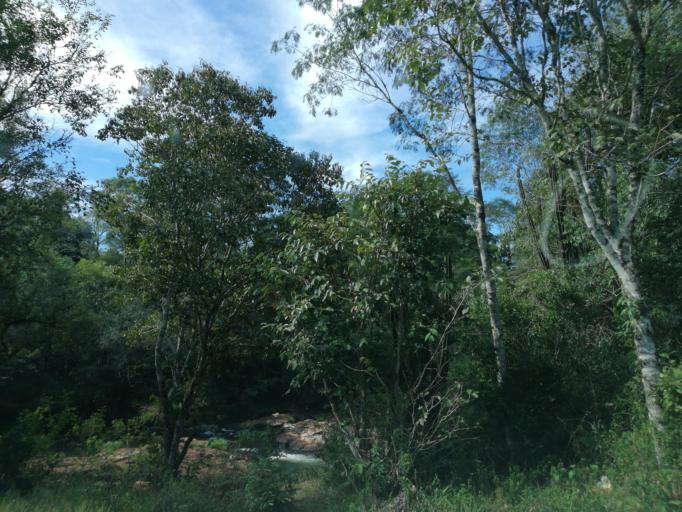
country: AR
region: Misiones
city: Dos de Mayo
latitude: -27.0157
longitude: -54.4148
